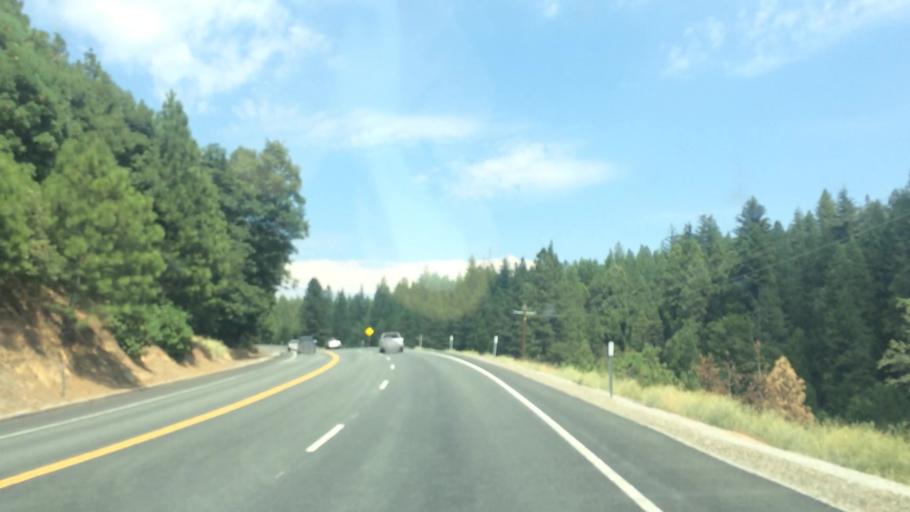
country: US
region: California
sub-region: Amador County
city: Pioneer
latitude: 38.4359
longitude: -120.5483
